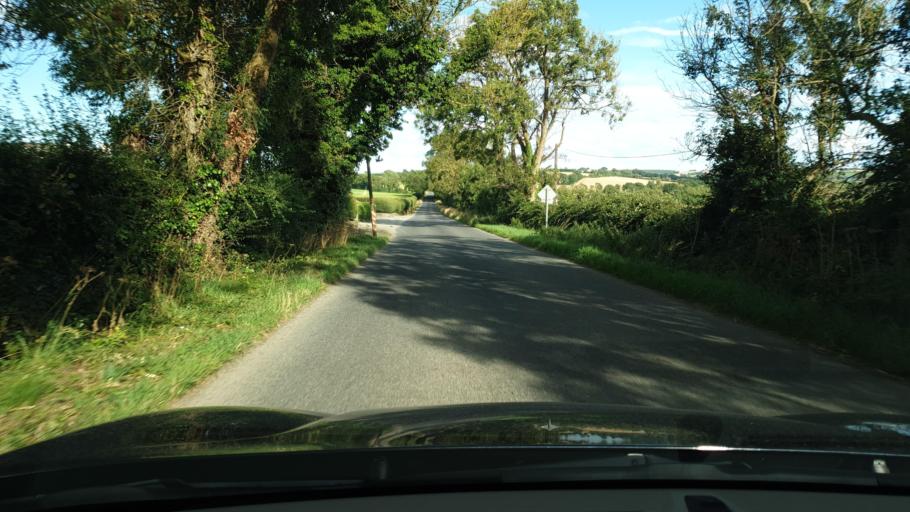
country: IE
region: Leinster
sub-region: An Mhi
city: Stamullin
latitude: 53.6243
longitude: -6.3441
